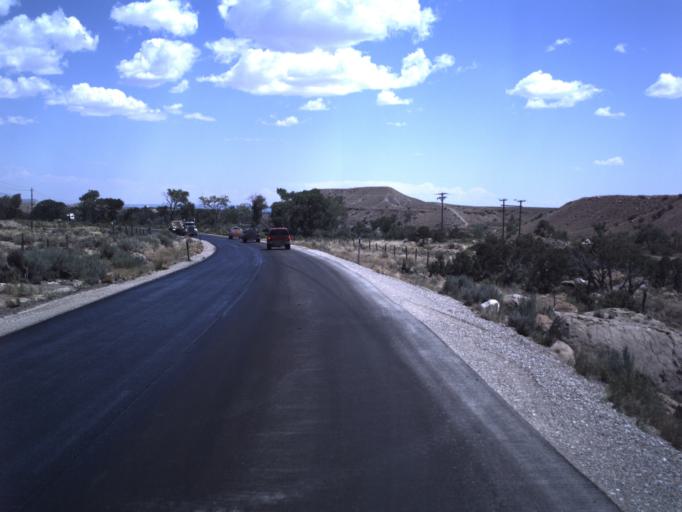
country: US
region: Utah
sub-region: Emery County
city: Orangeville
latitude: 39.2516
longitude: -111.0928
